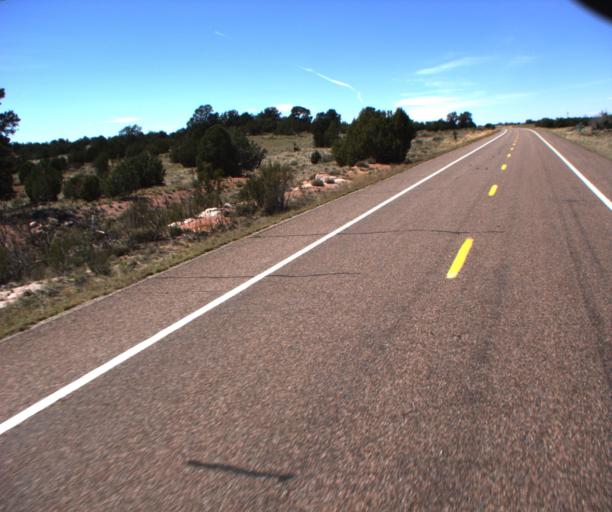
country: US
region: Arizona
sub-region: Mohave County
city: Peach Springs
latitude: 35.5115
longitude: -113.1899
